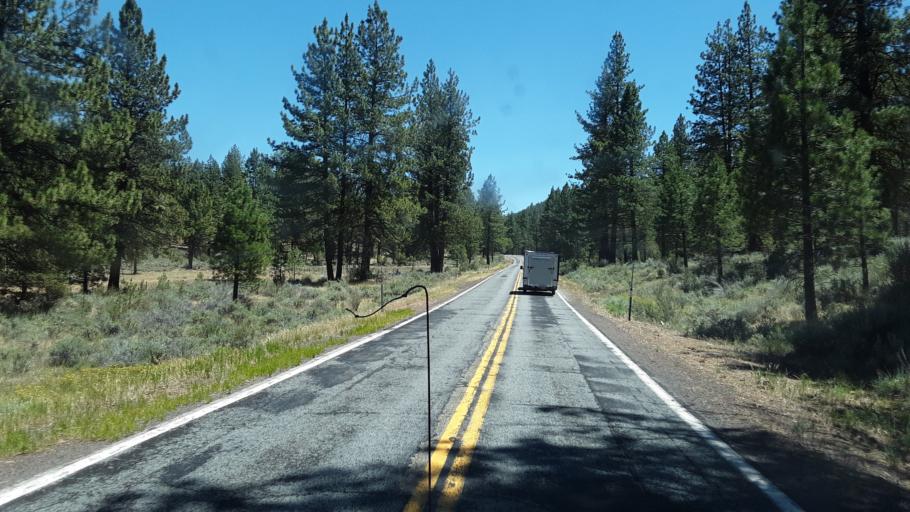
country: US
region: California
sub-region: Modoc County
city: Alturas
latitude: 40.9831
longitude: -120.7941
